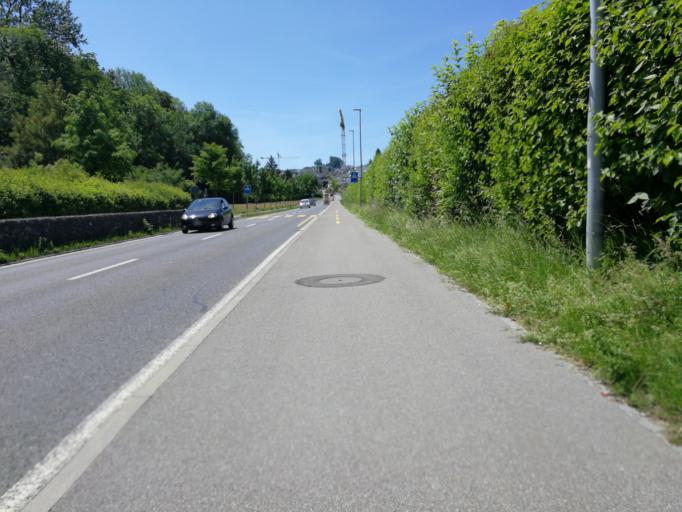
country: CH
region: Schwyz
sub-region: Bezirk Hoefe
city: Freienbach
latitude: 47.2002
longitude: 8.7483
